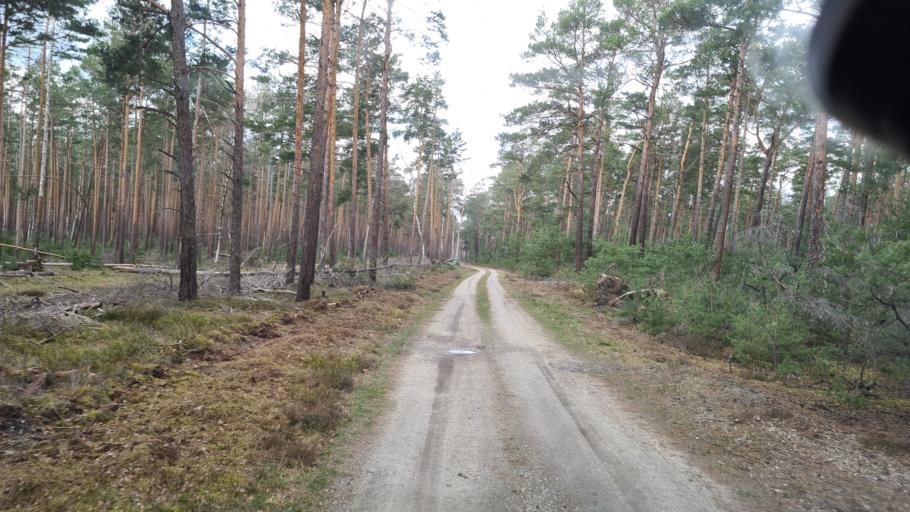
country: DE
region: Brandenburg
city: Schonborn
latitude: 51.6459
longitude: 13.4844
